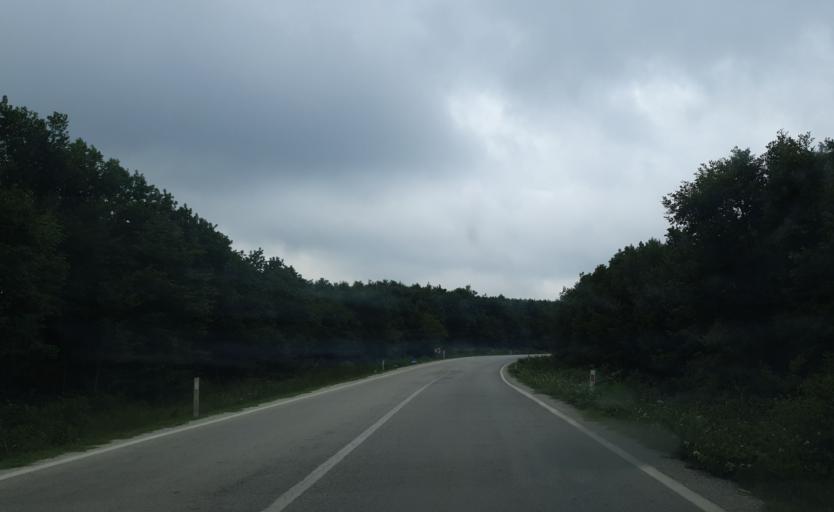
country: TR
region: Kirklareli
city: Salmydessus
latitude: 41.5751
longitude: 28.0749
